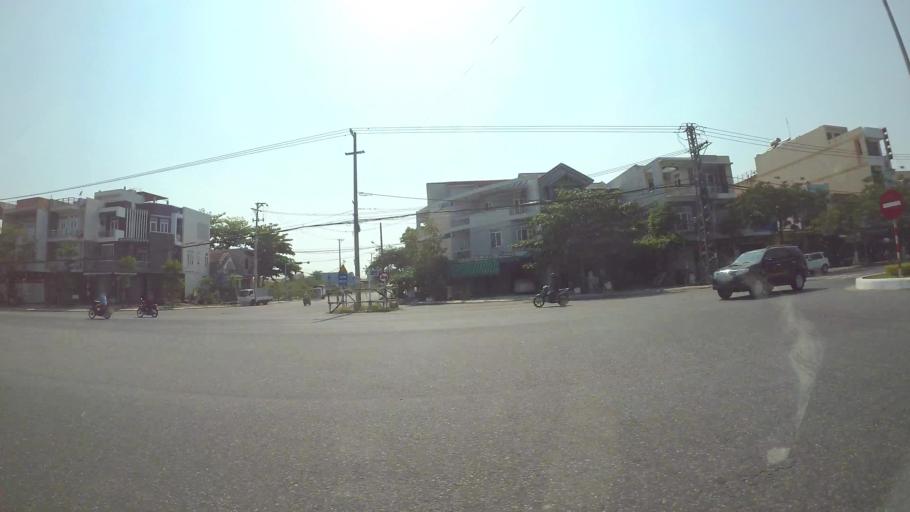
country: VN
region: Da Nang
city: Ngu Hanh Son
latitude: 16.0264
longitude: 108.2491
